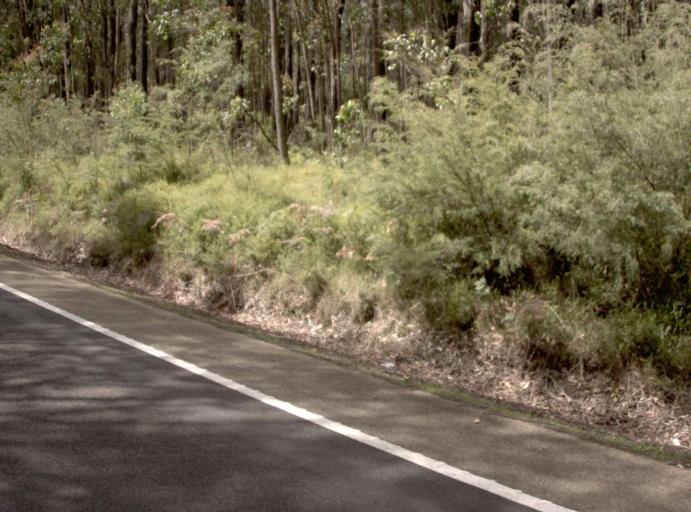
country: AU
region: New South Wales
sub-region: Bombala
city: Bombala
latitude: -37.5408
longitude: 149.3681
